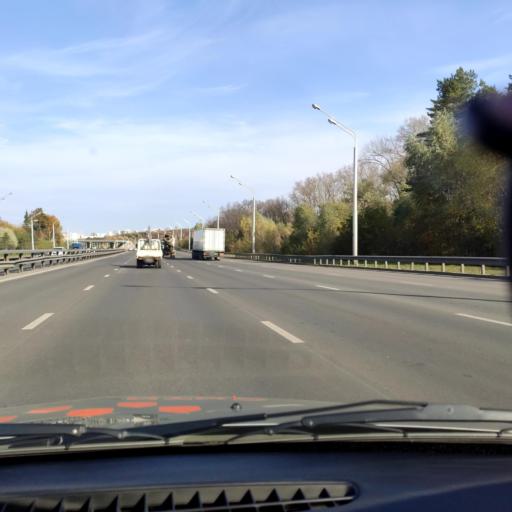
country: RU
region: Bashkortostan
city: Ufa
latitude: 54.7335
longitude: 56.0038
